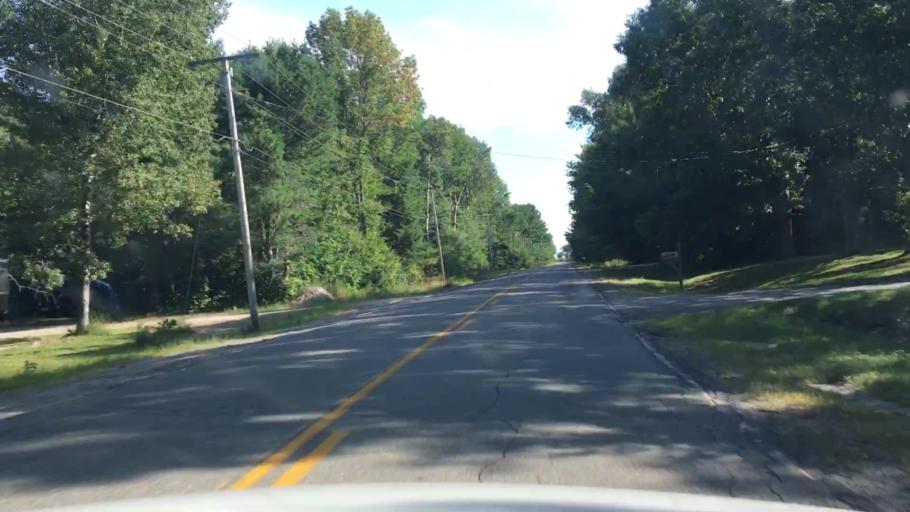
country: US
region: Maine
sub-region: Penobscot County
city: Enfield
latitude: 45.2350
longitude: -68.5441
